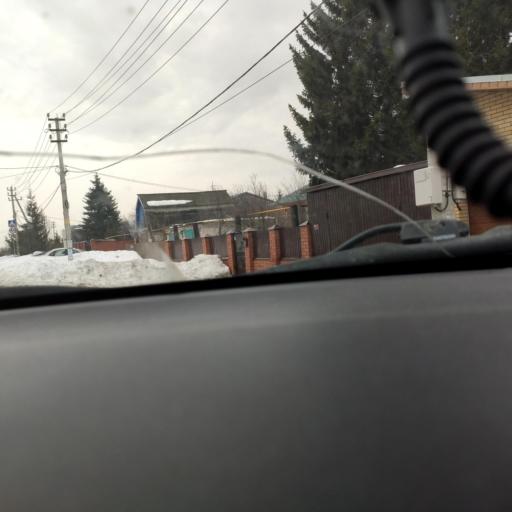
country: RU
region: Tatarstan
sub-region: Gorod Kazan'
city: Kazan
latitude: 55.8986
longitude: 49.1395
